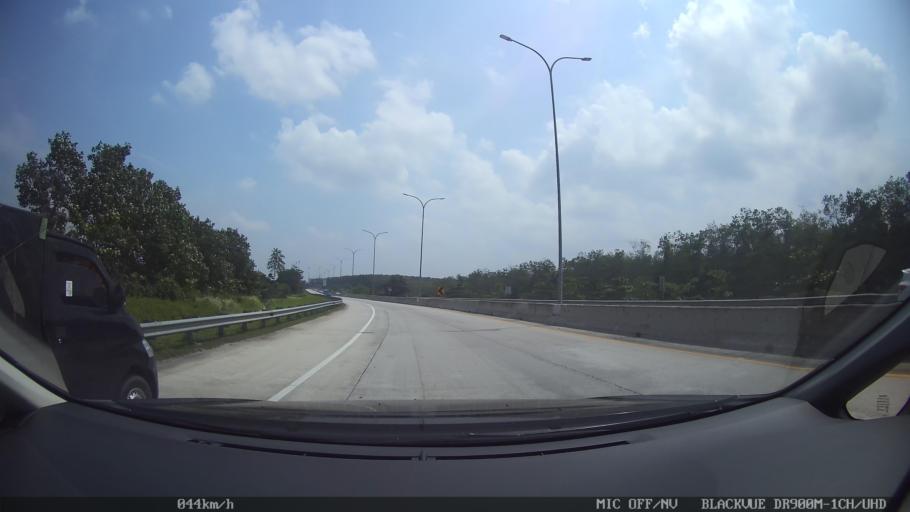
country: ID
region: Lampung
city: Kedaton
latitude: -5.3640
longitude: 105.3276
